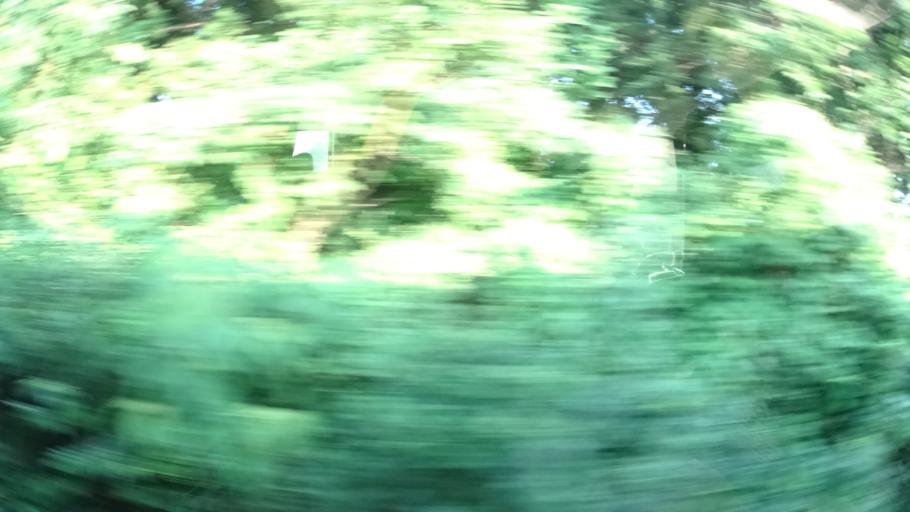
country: JP
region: Ibaraki
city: Funaishikawa
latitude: 36.4588
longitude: 140.5574
